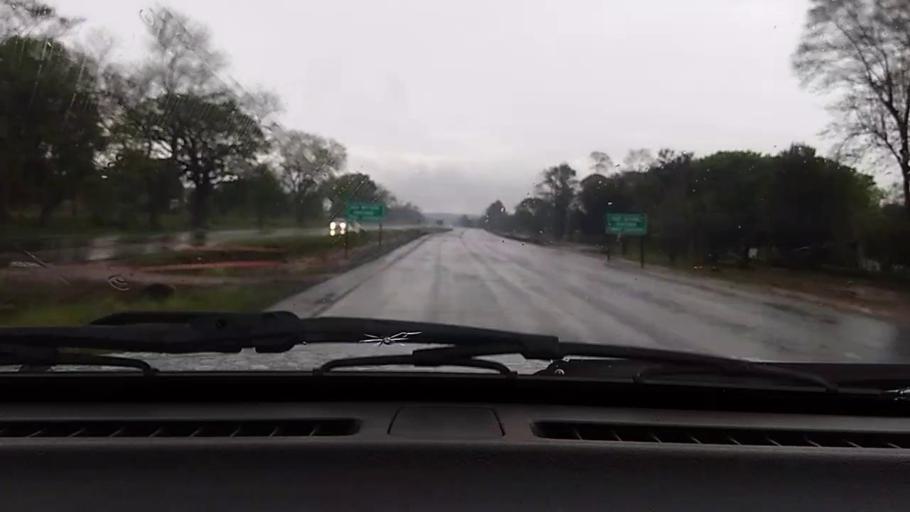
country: PY
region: Caaguazu
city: Repatriacion
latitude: -25.4592
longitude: -55.9210
